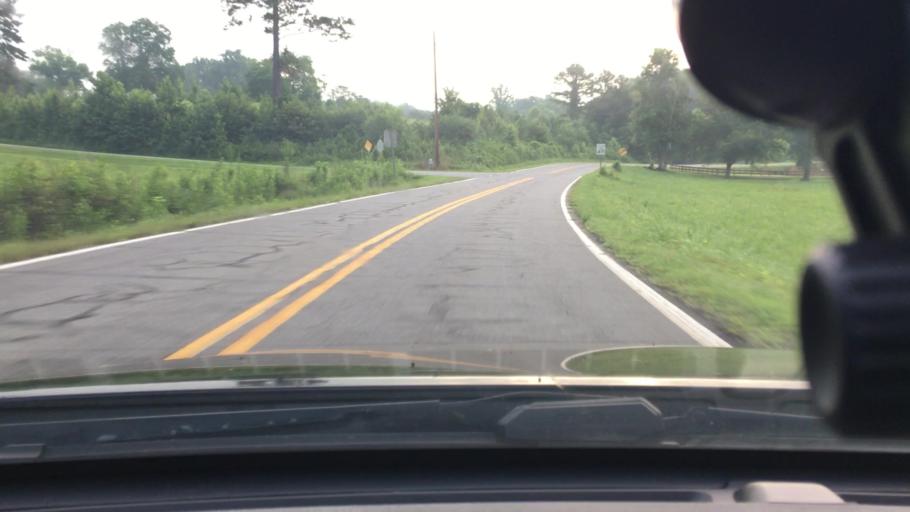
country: US
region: North Carolina
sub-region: Rutherford County
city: Rutherfordton
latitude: 35.3780
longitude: -81.9829
